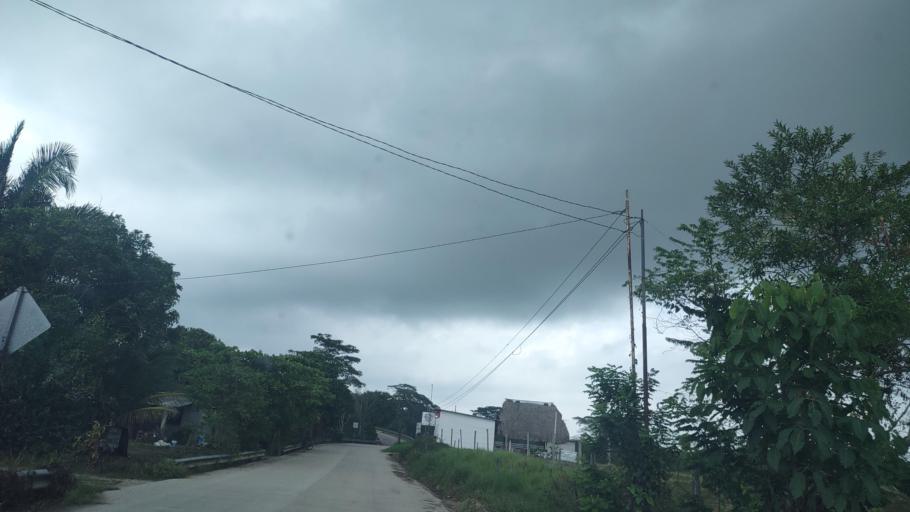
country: MX
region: Veracruz
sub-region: Uxpanapa
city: Poblado 10
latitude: 17.4946
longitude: -94.1658
